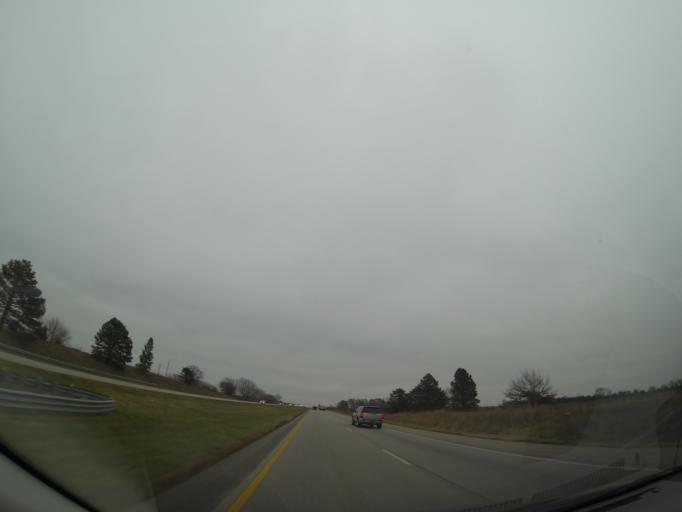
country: US
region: Nebraska
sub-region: Seward County
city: Milford
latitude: 40.8209
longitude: -97.0058
